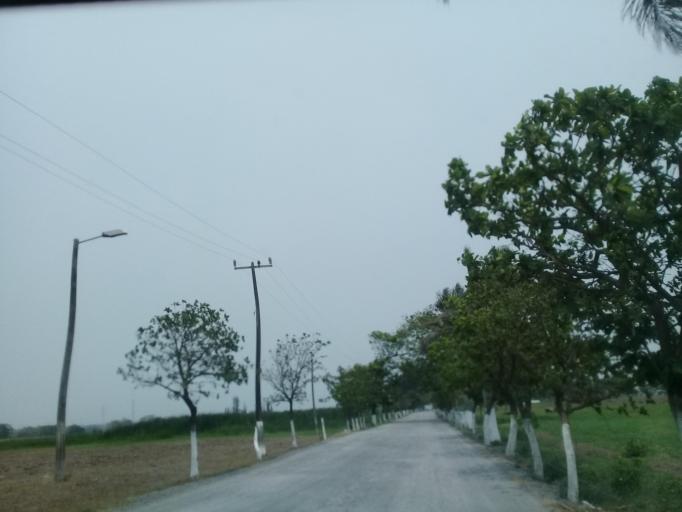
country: MX
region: Veracruz
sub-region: Veracruz
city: Las Amapolas
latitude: 19.1693
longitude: -96.2108
